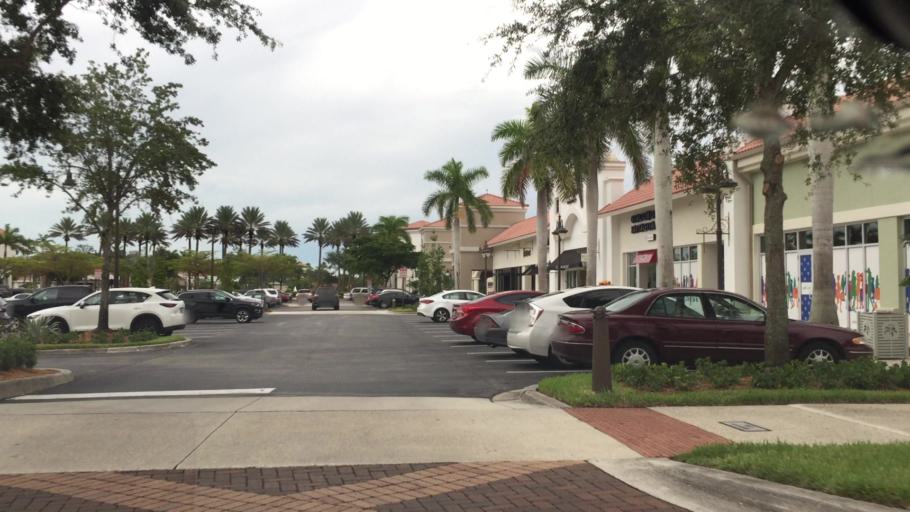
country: US
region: Florida
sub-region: Lee County
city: Three Oaks
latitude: 26.4868
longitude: -81.7899
